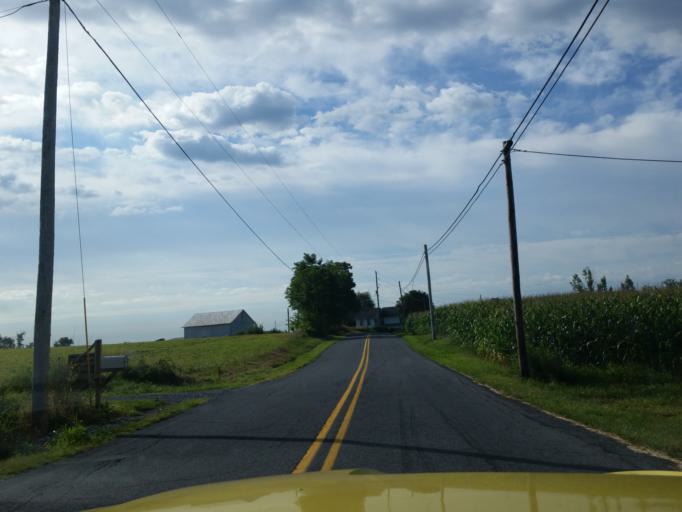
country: US
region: Pennsylvania
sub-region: Lebanon County
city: Fredericksburg
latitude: 40.4556
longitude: -76.4351
